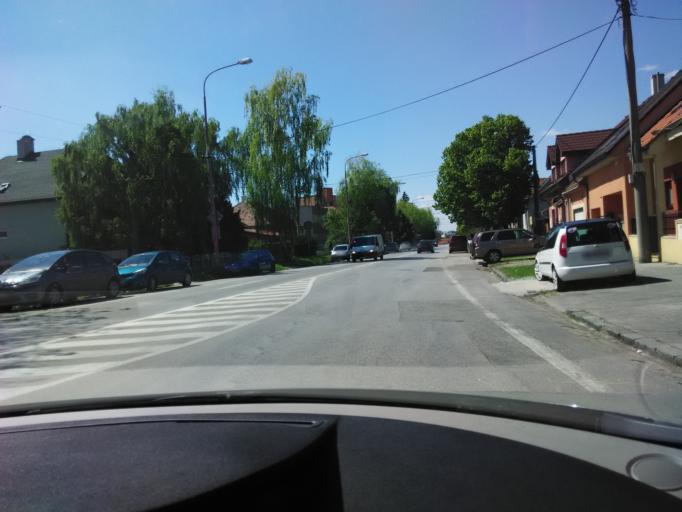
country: SK
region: Trnavsky
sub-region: Okres Trnava
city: Trnava
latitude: 48.3908
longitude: 17.5956
